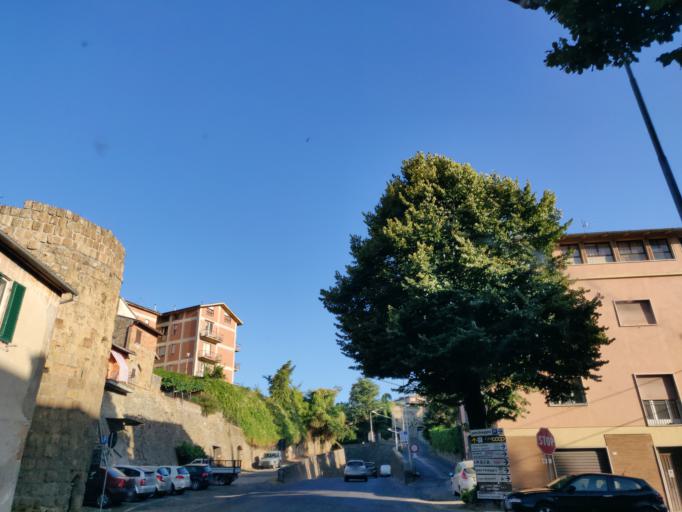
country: IT
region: Latium
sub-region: Provincia di Viterbo
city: Acquapendente
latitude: 42.7433
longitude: 11.8633
